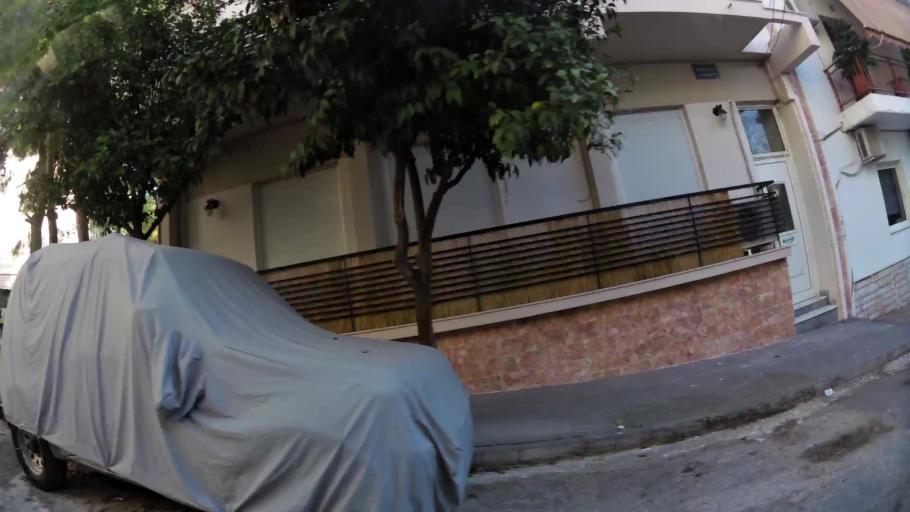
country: GR
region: Attica
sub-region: Nomos Piraios
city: Keratsini
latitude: 37.9729
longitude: 23.6281
